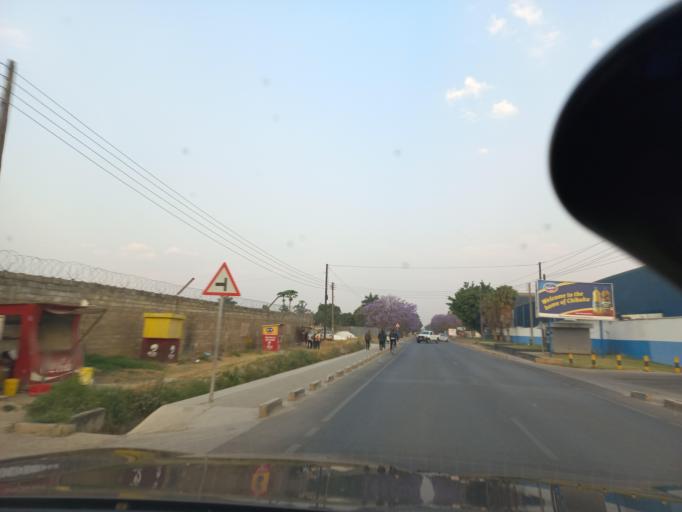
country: ZM
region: Lusaka
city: Lusaka
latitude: -15.3939
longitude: 28.2728
